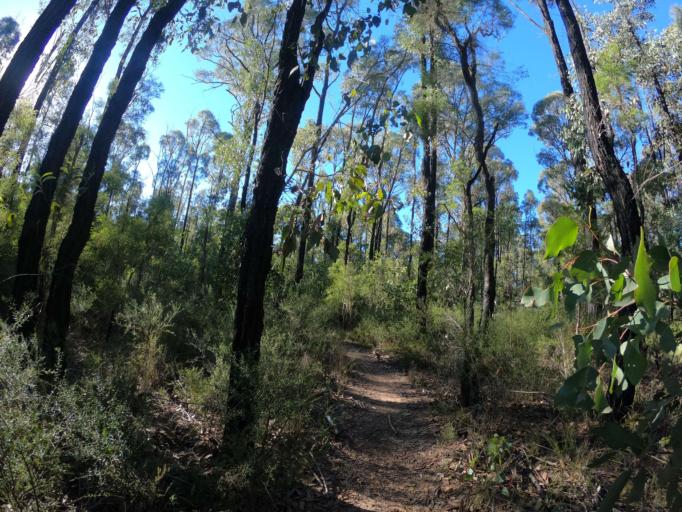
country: AU
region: New South Wales
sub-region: Hawkesbury
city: South Windsor
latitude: -33.6431
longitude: 150.7927
